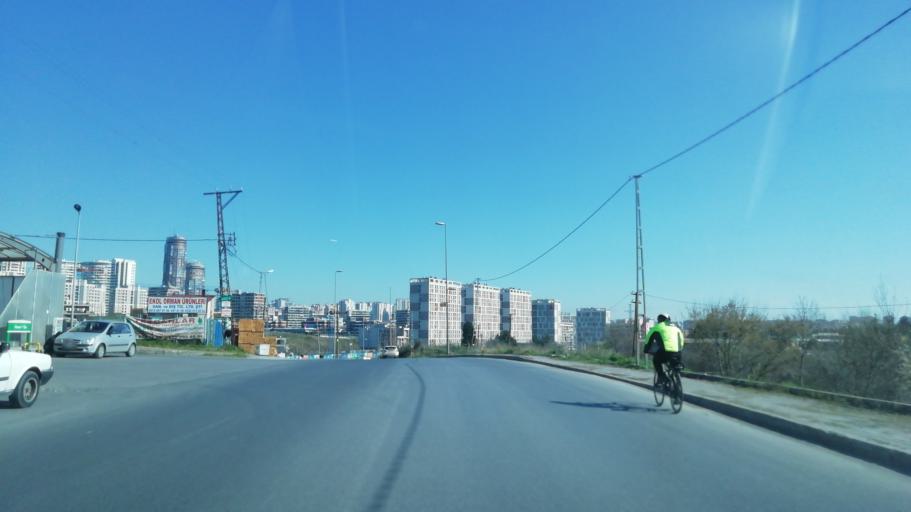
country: TR
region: Istanbul
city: Basaksehir
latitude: 41.0425
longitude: 28.7562
